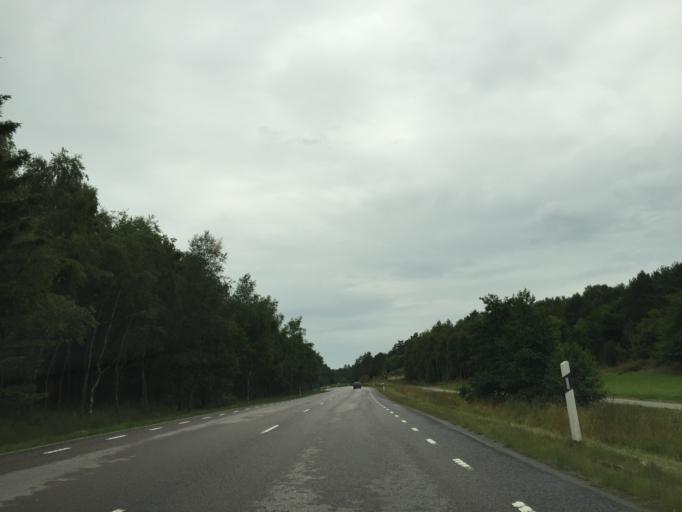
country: SE
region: Vaestra Goetaland
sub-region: Tjorns Kommun
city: Myggenas
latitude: 58.0235
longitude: 11.6866
